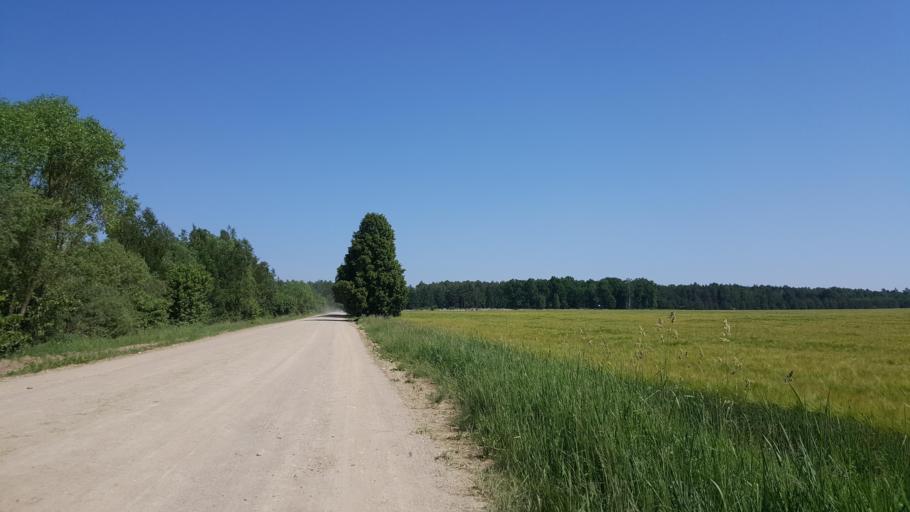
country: BY
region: Brest
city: Zhabinka
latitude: 52.2398
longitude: 24.0077
